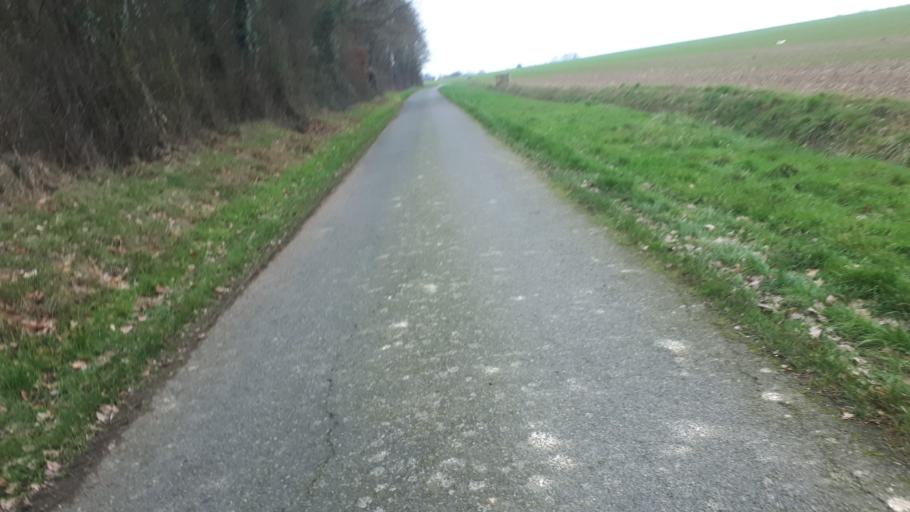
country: FR
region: Centre
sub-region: Departement du Loir-et-Cher
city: Villiers-sur-Loir
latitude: 47.8175
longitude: 0.9989
